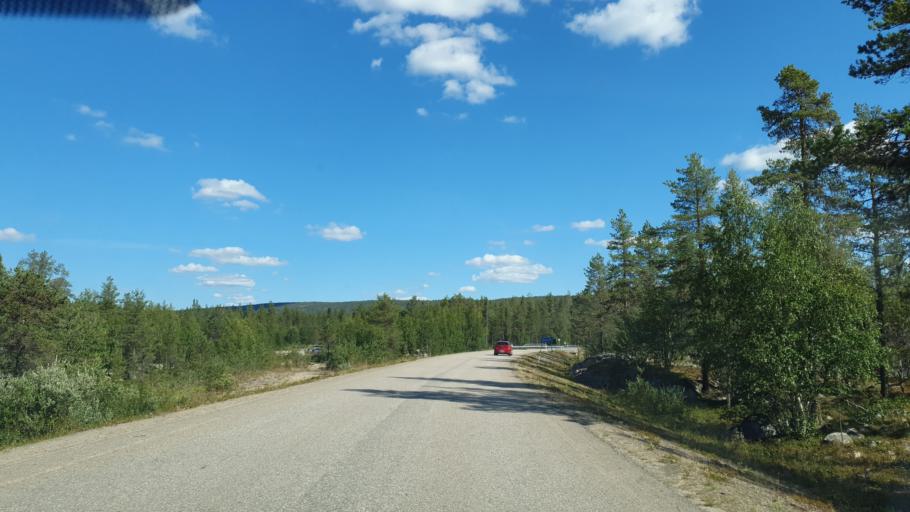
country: FI
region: Lapland
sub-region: Tunturi-Lappi
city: Muonio
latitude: 67.7051
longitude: 24.1240
